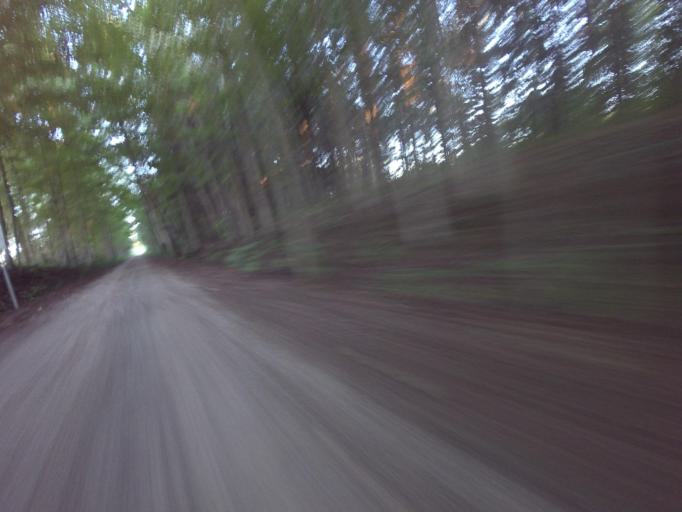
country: CA
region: Ontario
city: Goderich
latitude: 43.7492
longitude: -81.6528
